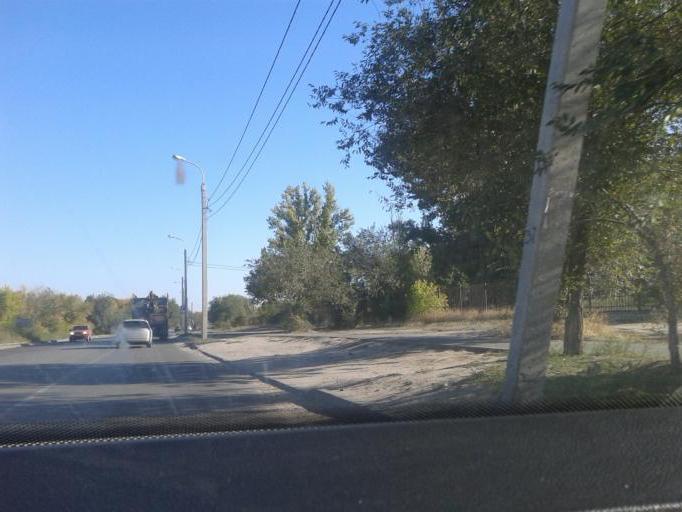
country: RU
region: Volgograd
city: Volgograd
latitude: 48.7635
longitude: 44.5178
